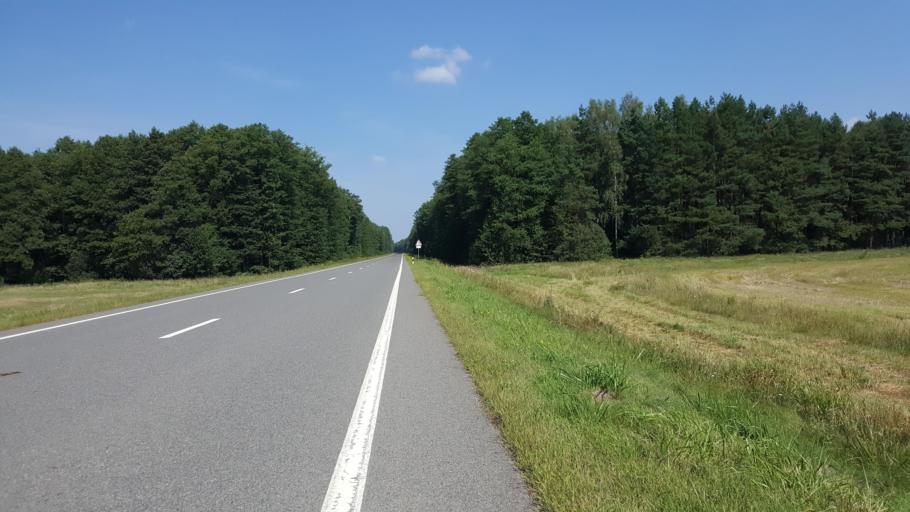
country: BY
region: Brest
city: Kamyanyuki
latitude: 52.5279
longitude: 23.6558
